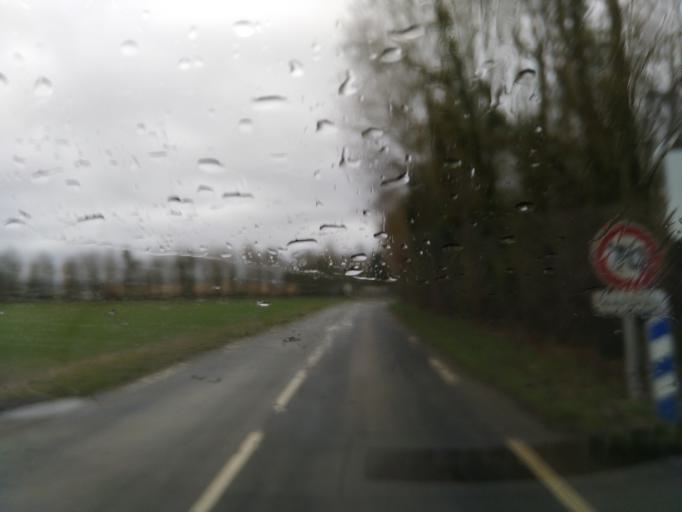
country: FR
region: Ile-de-France
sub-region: Departement des Yvelines
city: Beynes
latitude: 48.8577
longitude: 1.8525
